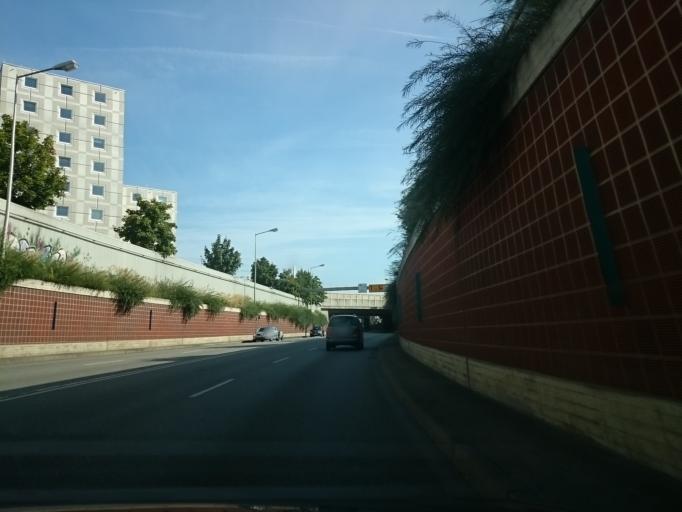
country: DE
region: Bavaria
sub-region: Swabia
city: Augsburg
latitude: 48.3531
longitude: 10.9054
